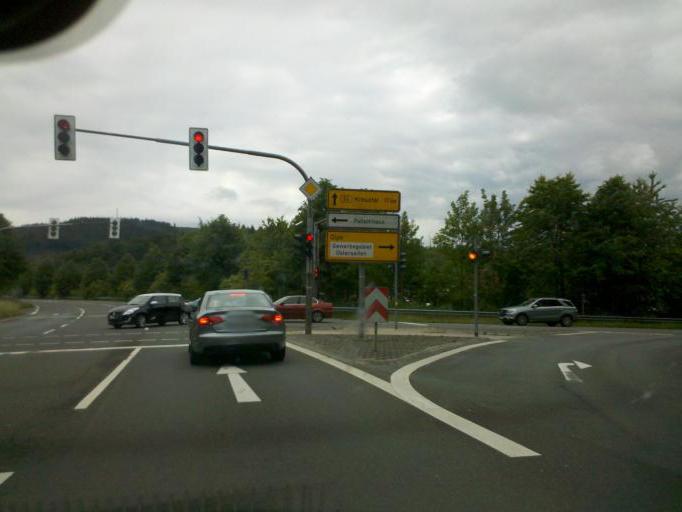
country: DE
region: North Rhine-Westphalia
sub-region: Regierungsbezirk Arnsberg
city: Olpe
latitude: 51.0407
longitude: 7.8628
